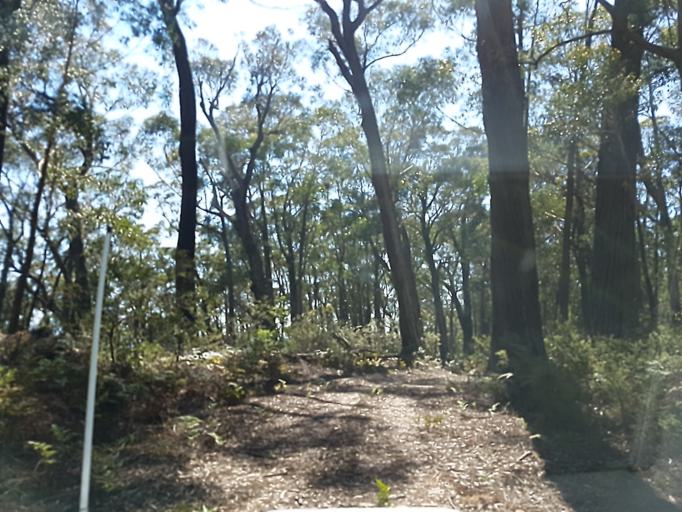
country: AU
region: Victoria
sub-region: East Gippsland
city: Lakes Entrance
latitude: -37.2903
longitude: 148.3216
